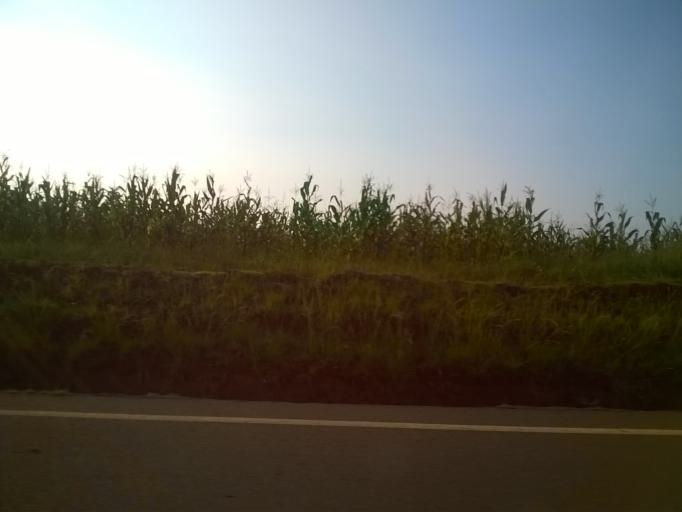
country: LS
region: Leribe
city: Leribe
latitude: -29.0335
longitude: 28.2532
